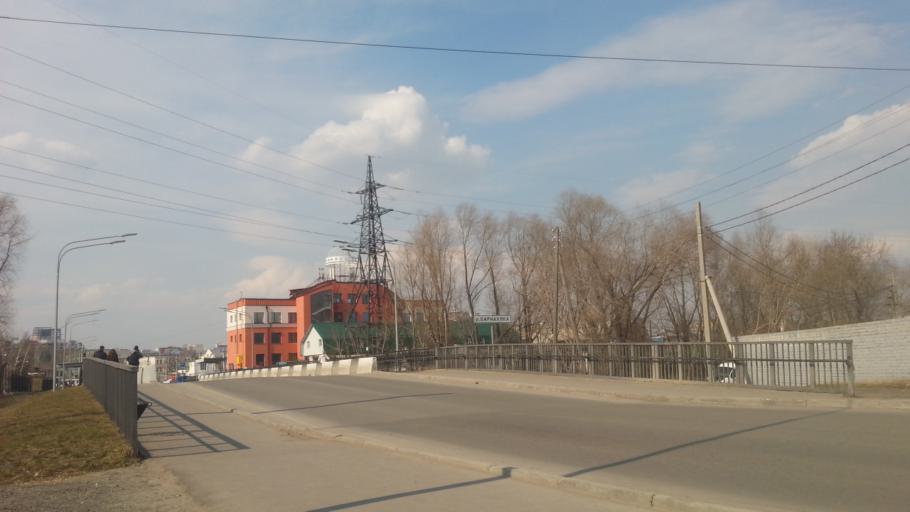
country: RU
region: Altai Krai
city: Zaton
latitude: 53.3272
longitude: 83.7924
